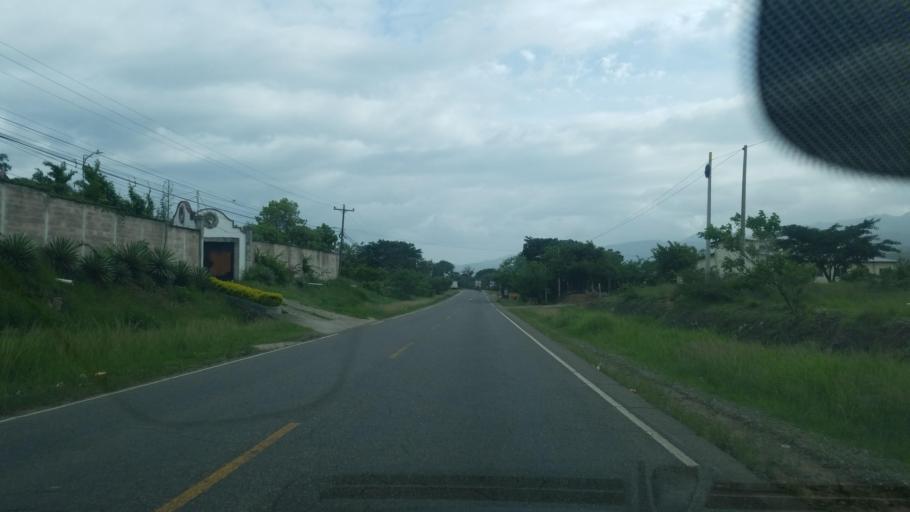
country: HN
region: Ocotepeque
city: Nueva Ocotepeque
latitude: 14.4240
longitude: -89.1857
